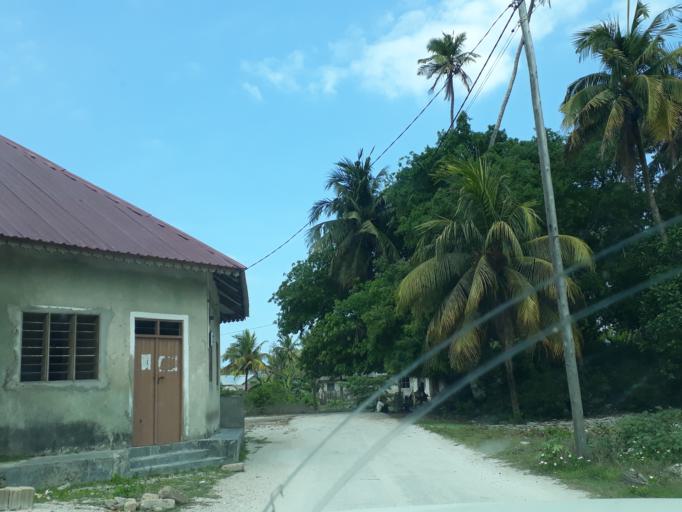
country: TZ
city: Kiwengwa
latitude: -6.0418
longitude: 39.4066
